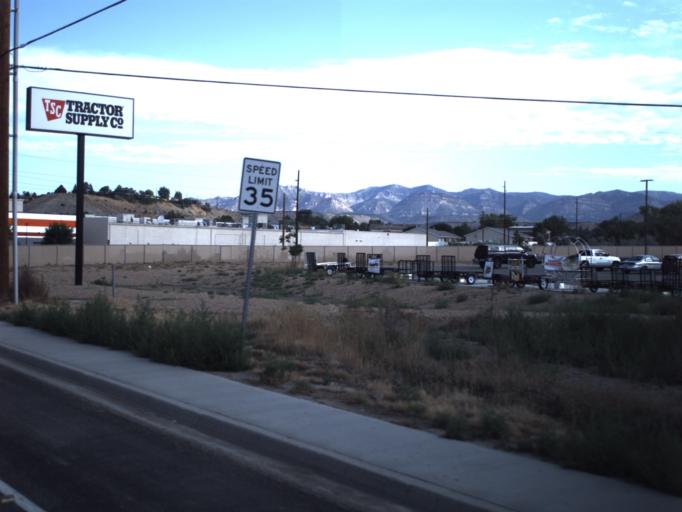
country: US
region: Utah
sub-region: Carbon County
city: Price
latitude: 39.5979
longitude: -110.7923
